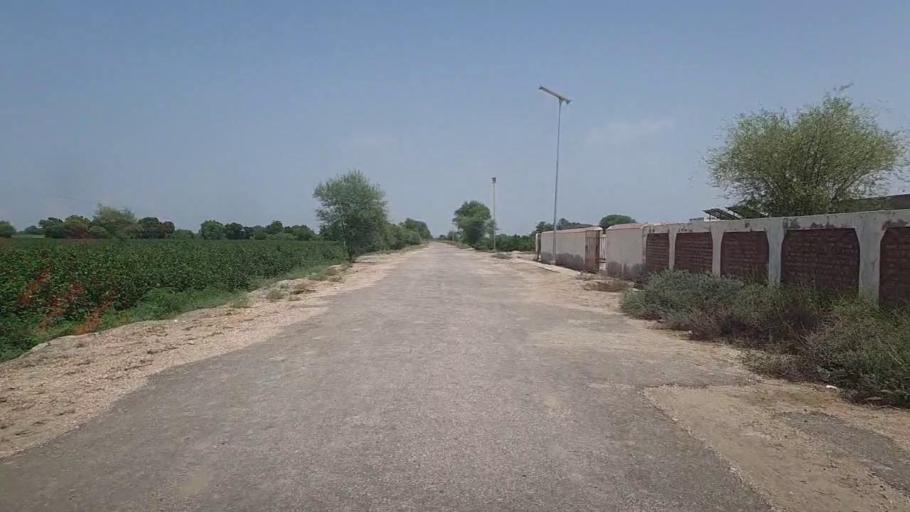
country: PK
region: Sindh
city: Pad Idan
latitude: 26.8445
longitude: 68.3248
